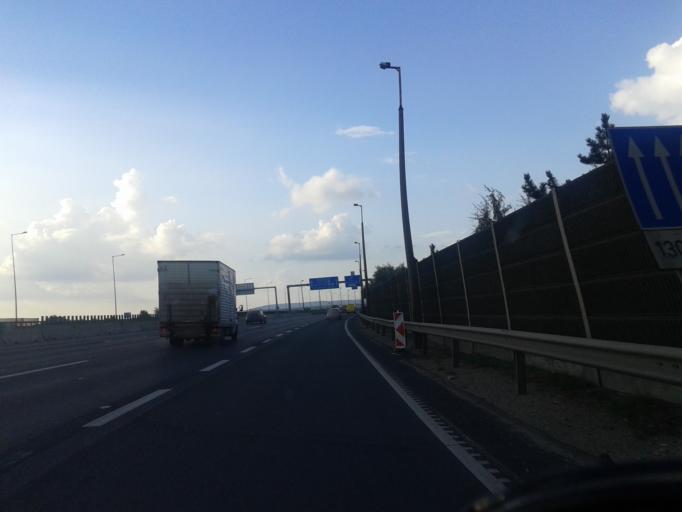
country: HU
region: Pest
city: Halasztelek
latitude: 47.3841
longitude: 19.0158
